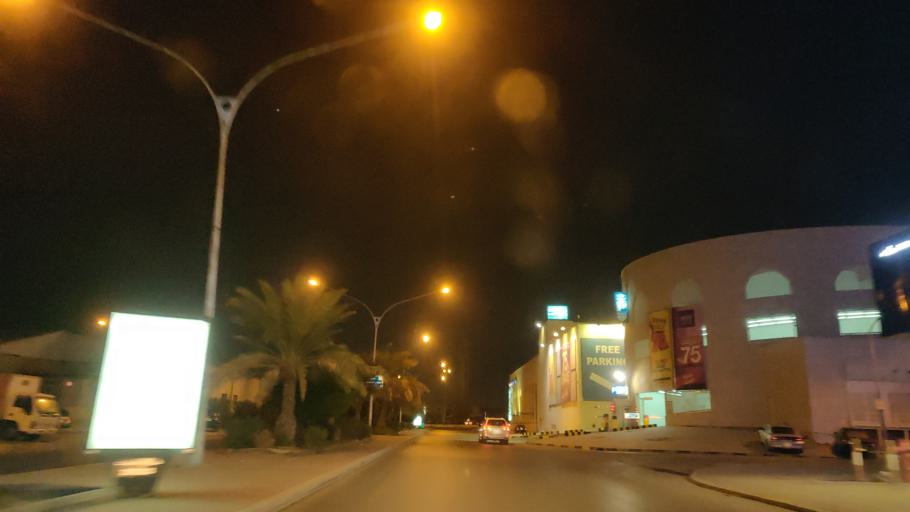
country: KW
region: Al Asimah
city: Ar Rabiyah
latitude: 29.3120
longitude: 47.9345
